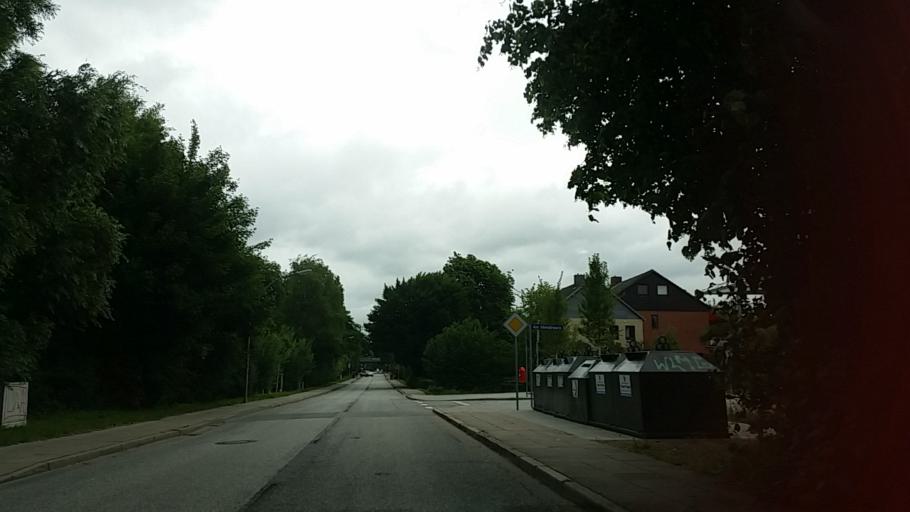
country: DE
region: Schleswig-Holstein
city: Oststeinbek
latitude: 53.4953
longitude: 10.1289
